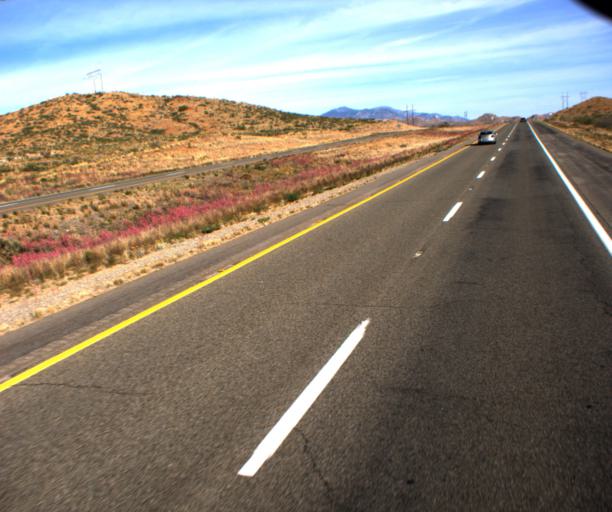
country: US
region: Arizona
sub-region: Cochise County
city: Willcox
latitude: 32.4612
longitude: -109.6675
